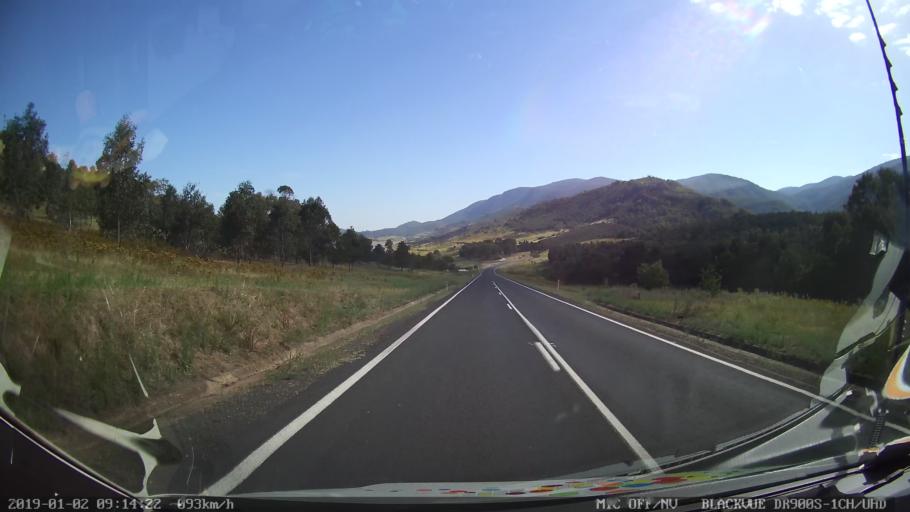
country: AU
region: New South Wales
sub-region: Tumut Shire
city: Tumut
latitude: -35.4781
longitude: 148.2735
